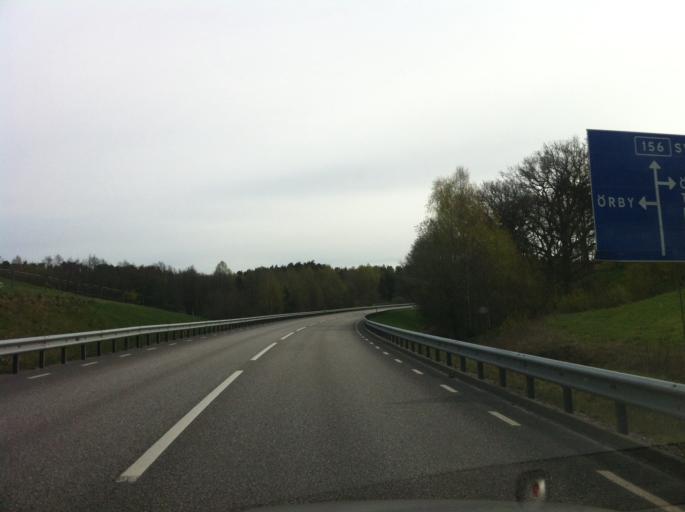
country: SE
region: Vaestra Goetaland
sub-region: Marks Kommun
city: Kinna
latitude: 57.4788
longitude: 12.6902
